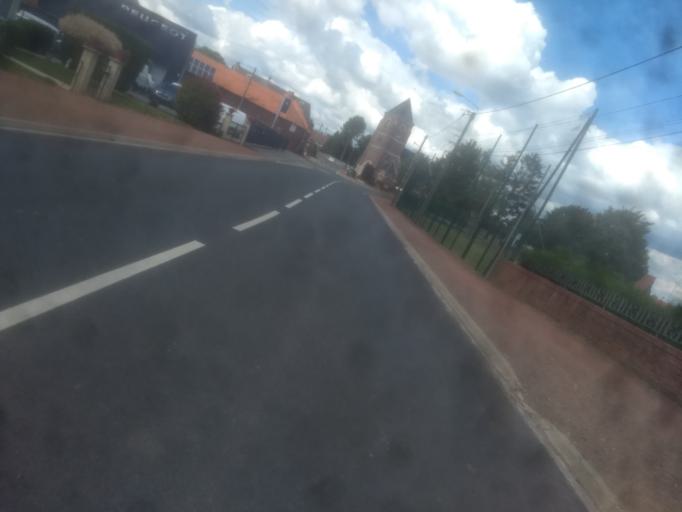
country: FR
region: Nord-Pas-de-Calais
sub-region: Departement du Pas-de-Calais
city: Croisilles
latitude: 50.2229
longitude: 2.8322
